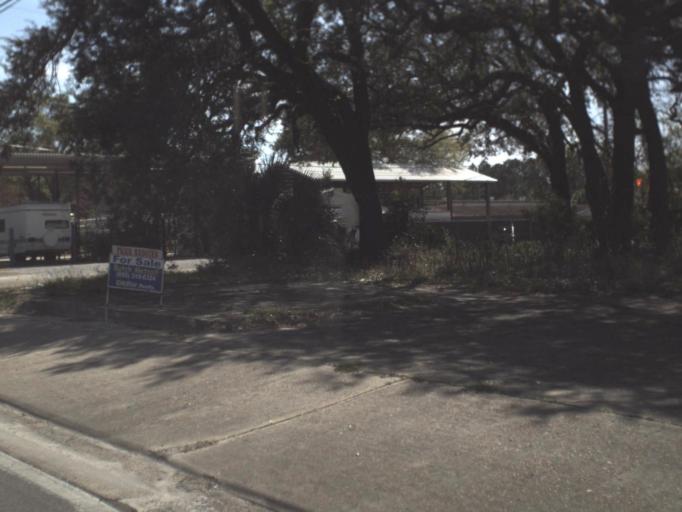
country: US
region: Florida
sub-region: Bay County
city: Lynn Haven
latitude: 30.2364
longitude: -85.6489
